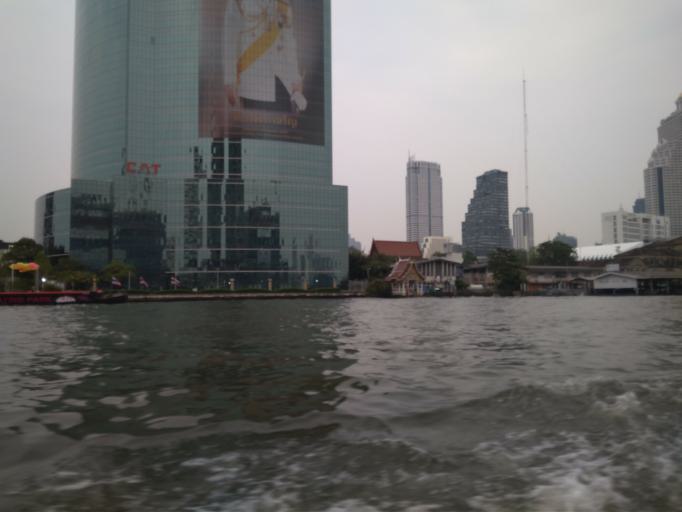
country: TH
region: Bangkok
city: Samphanthawong
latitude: 13.7268
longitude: 100.5126
